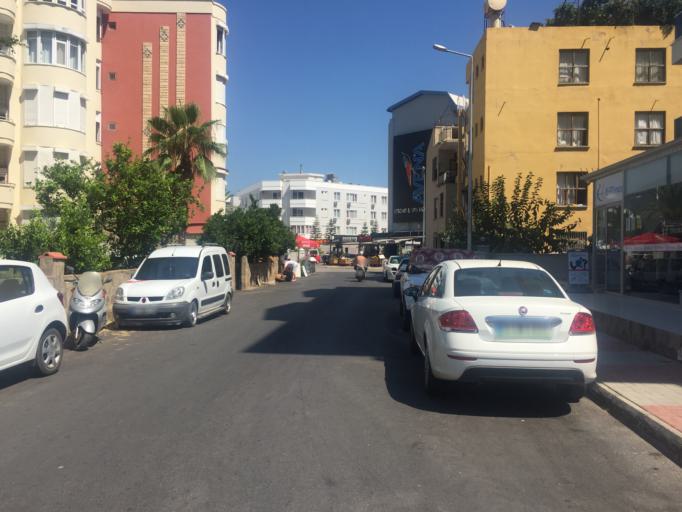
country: TR
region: Antalya
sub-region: Alanya
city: Alanya
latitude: 36.5373
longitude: 32.0357
